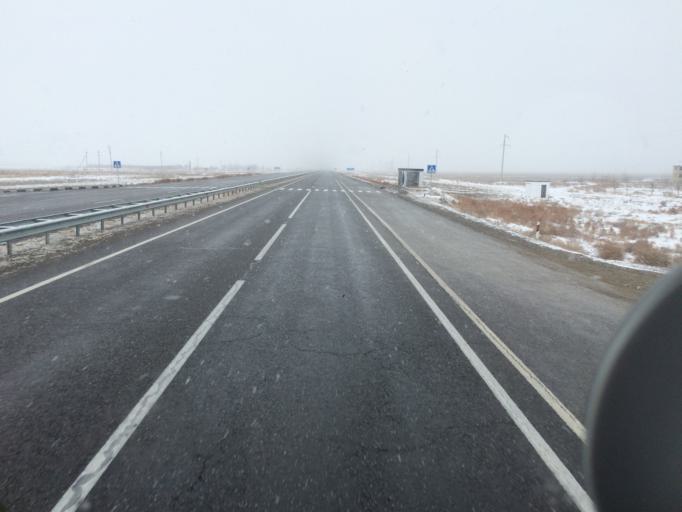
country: KZ
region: Ongtustik Qazaqstan
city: Turkestan
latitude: 43.4576
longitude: 67.9330
